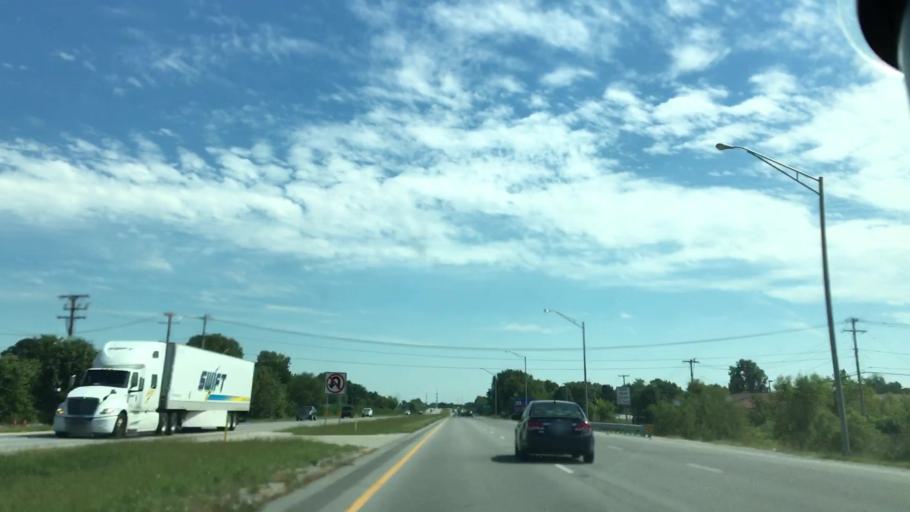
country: US
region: Kentucky
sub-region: Daviess County
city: Owensboro
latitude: 37.7397
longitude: -87.1449
